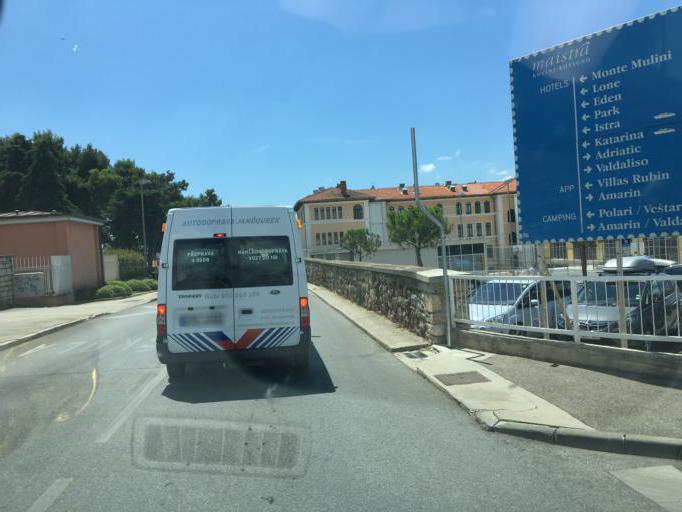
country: HR
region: Istarska
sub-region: Grad Rovinj
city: Rovinj
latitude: 45.0829
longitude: 13.6418
